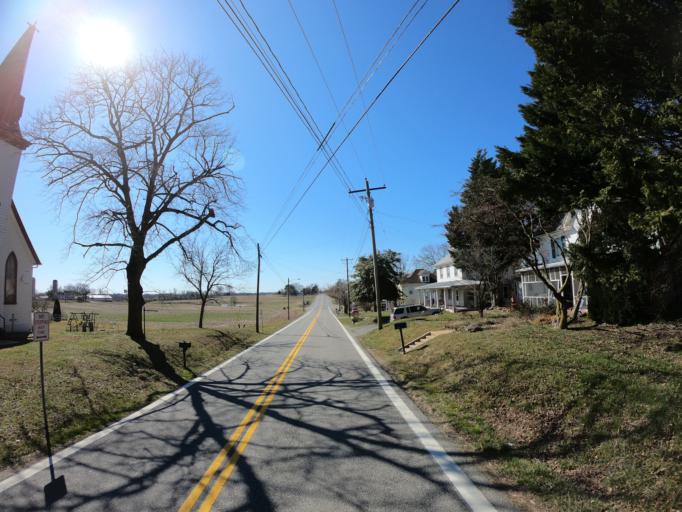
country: US
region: Maryland
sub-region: Queen Anne's County
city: Kingstown
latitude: 39.3046
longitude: -75.9961
